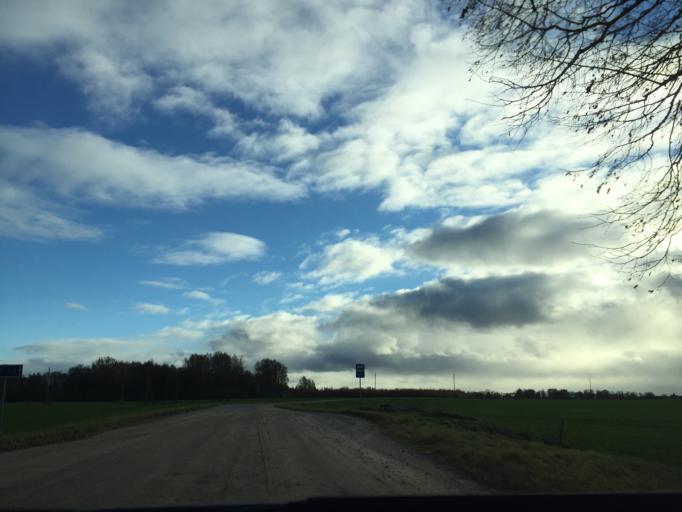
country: LV
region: Tukuma Rajons
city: Tukums
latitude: 56.9349
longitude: 22.9534
